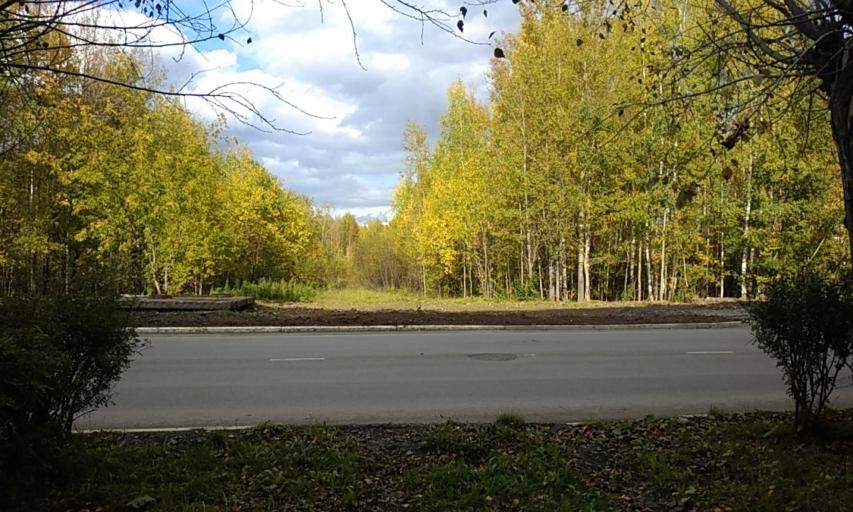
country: RU
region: Sverdlovsk
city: Krasnoural'sk
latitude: 58.3593
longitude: 60.0269
